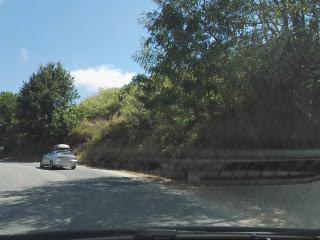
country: IT
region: Calabria
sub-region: Provincia di Vibo-Valentia
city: Spilinga
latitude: 38.6172
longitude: 15.8872
